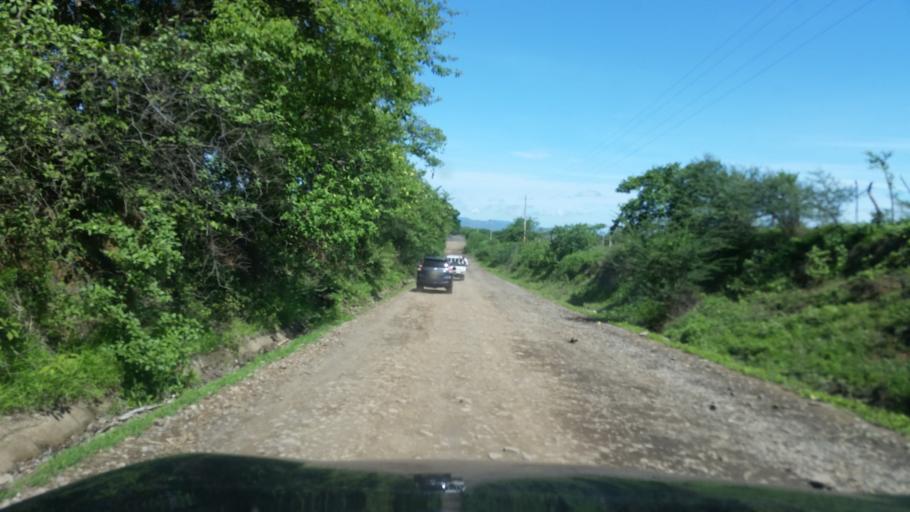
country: NI
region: Chinandega
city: Puerto Morazan
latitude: 12.7673
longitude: -87.0605
